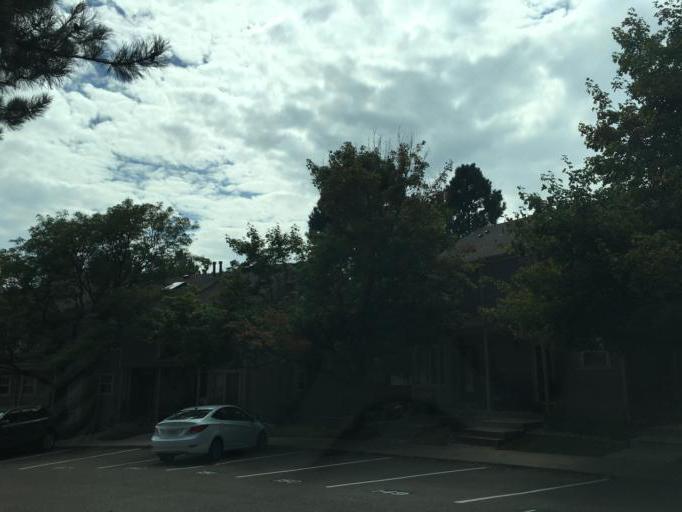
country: US
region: Colorado
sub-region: Jefferson County
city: Applewood
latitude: 39.7453
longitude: -105.1208
